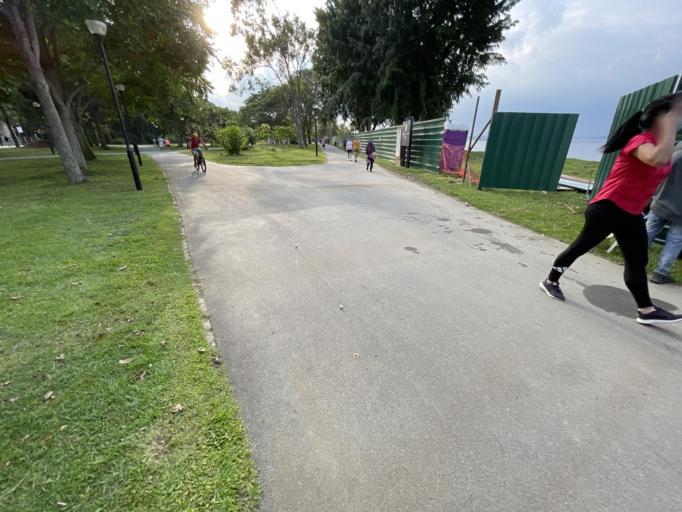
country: MY
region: Johor
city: Kampung Pasir Gudang Baru
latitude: 1.3809
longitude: 103.9600
